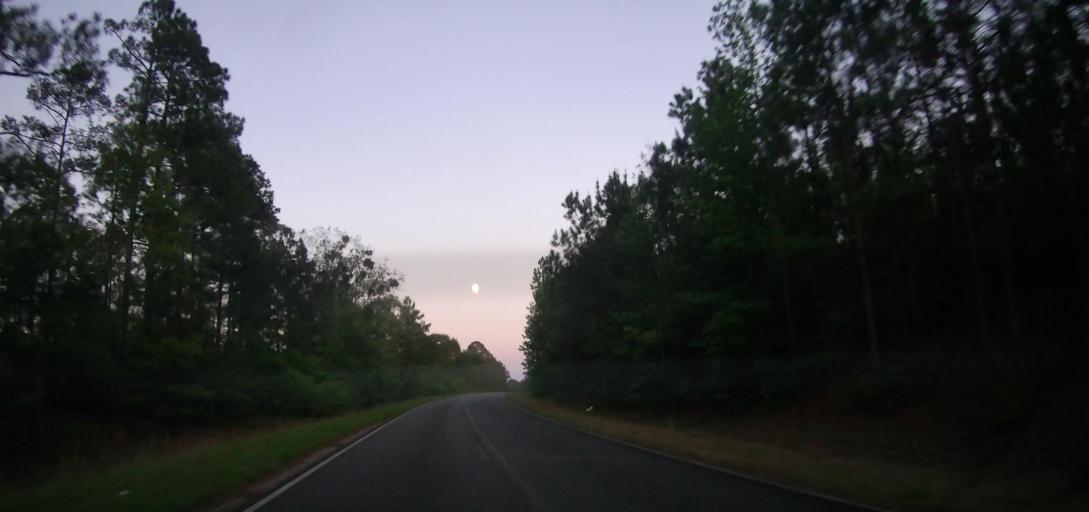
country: US
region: Georgia
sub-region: Marion County
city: Buena Vista
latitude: 32.2554
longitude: -84.6224
